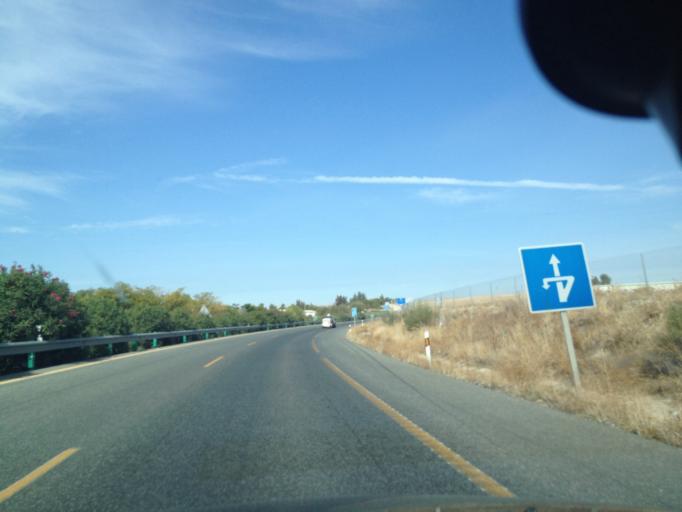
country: ES
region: Andalusia
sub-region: Provincia de Sevilla
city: La Puebla de Cazalla
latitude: 37.2268
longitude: -5.2975
